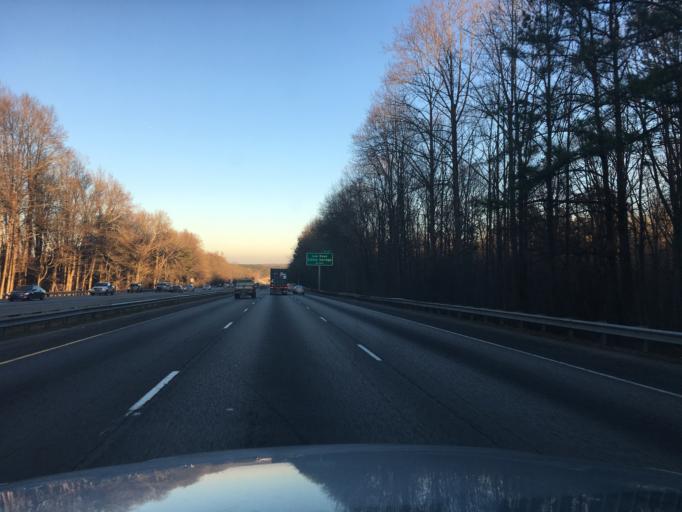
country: US
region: Georgia
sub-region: Douglas County
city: Lithia Springs
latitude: 33.7644
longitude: -84.6680
